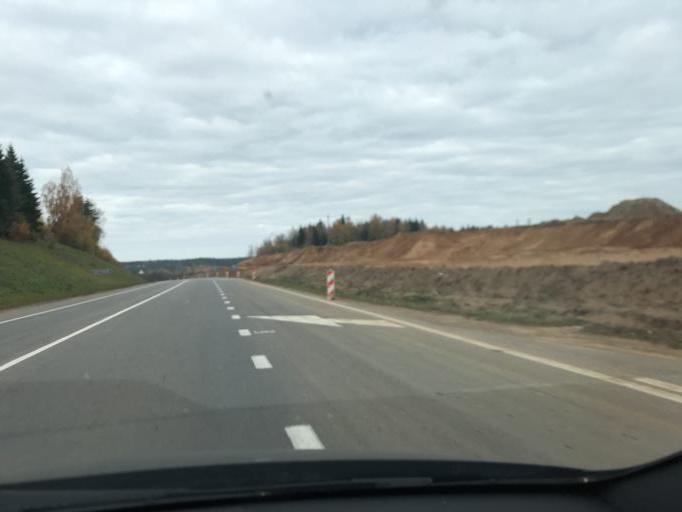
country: BY
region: Minsk
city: Slabada
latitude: 54.0311
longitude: 27.8691
